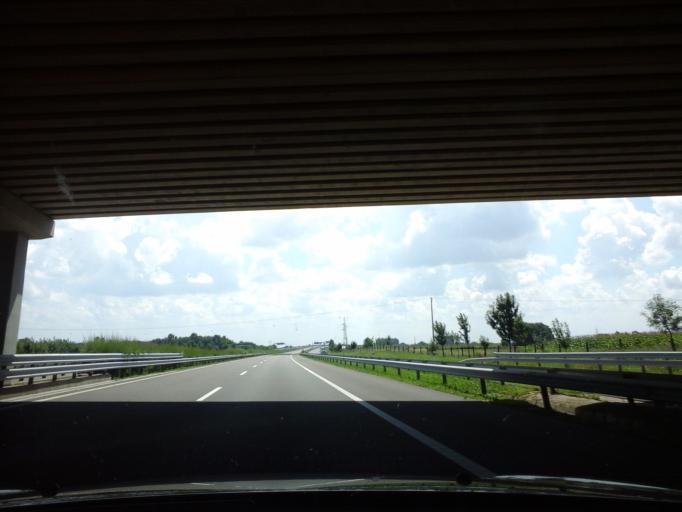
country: HU
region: Hajdu-Bihar
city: Debrecen
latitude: 47.5619
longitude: 21.5483
